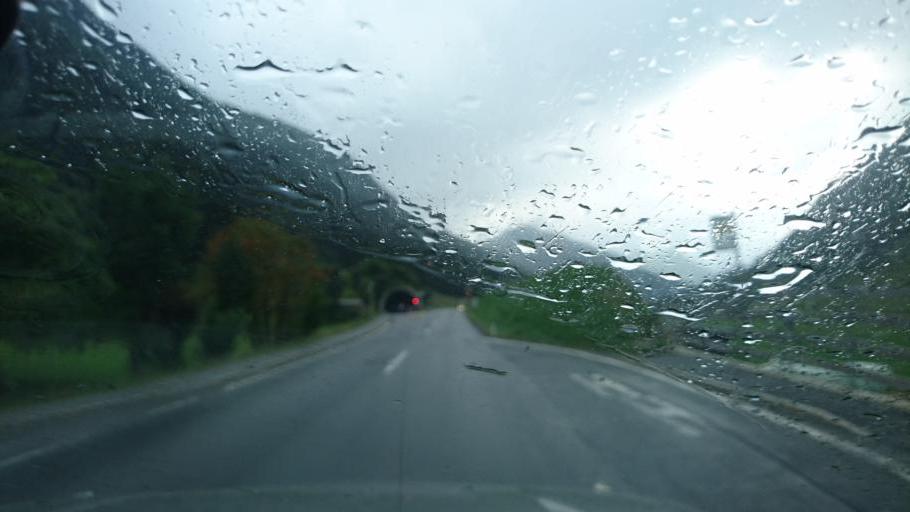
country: AT
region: Tyrol
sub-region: Politischer Bezirk Landeck
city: Ischgl
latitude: 47.0020
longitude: 10.2747
